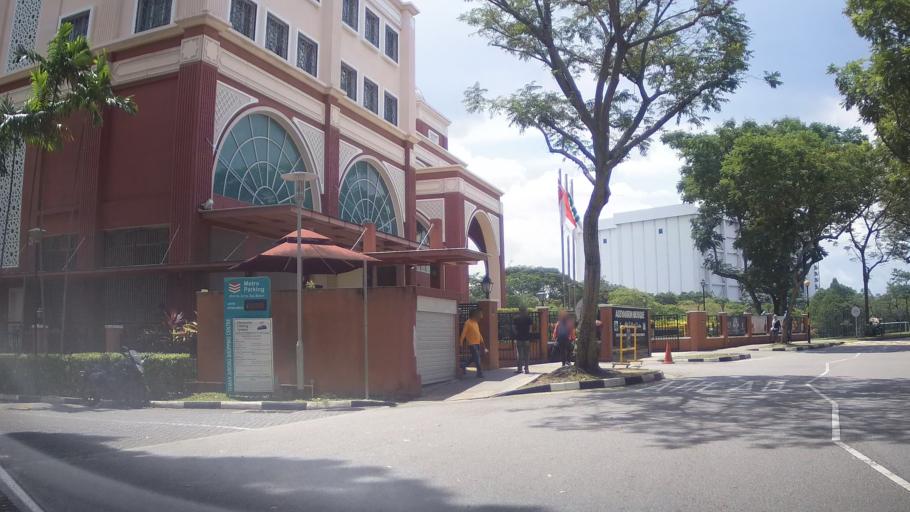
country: MY
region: Johor
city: Johor Bahru
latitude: 1.3356
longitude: 103.7201
